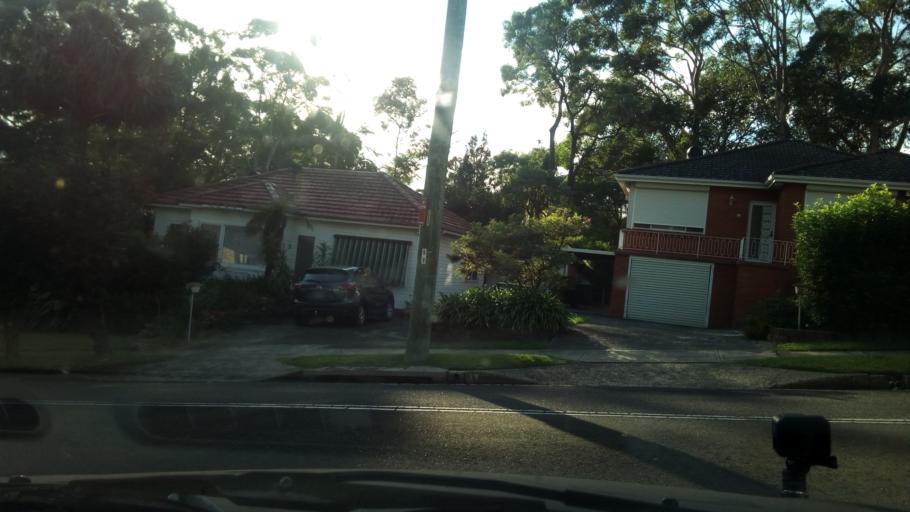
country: AU
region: New South Wales
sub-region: Wollongong
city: Mount Ousley
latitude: -34.3962
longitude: 150.8717
